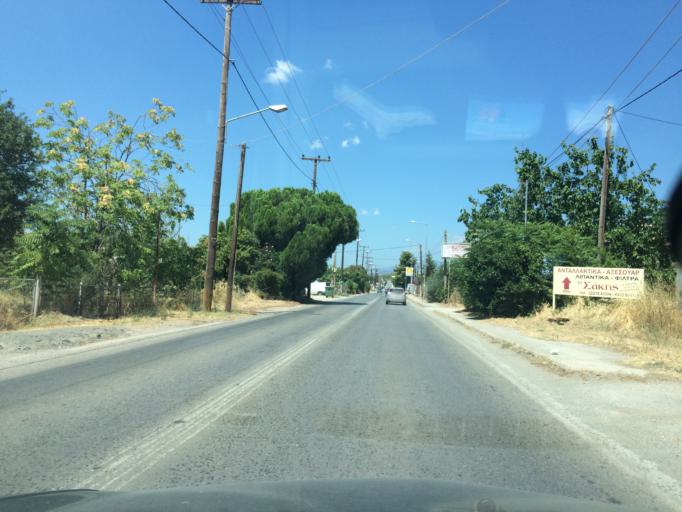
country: GR
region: Central Greece
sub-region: Nomos Evvoias
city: Nea Artaki
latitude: 38.5182
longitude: 23.6373
